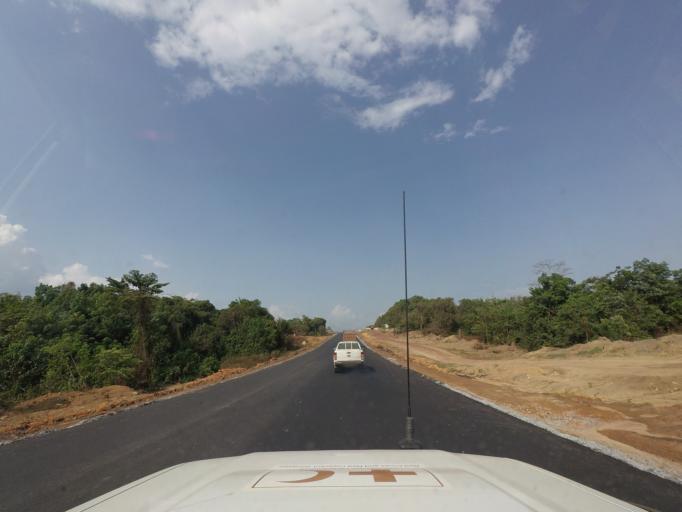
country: LR
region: Margibi
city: Kakata
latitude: 6.7404
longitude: -10.1199
